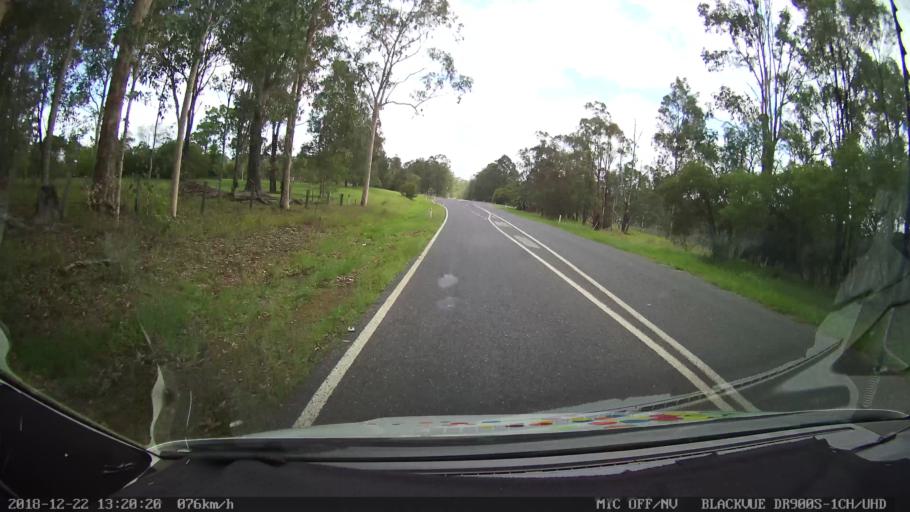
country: AU
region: New South Wales
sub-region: Clarence Valley
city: South Grafton
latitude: -29.7651
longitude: 152.9277
